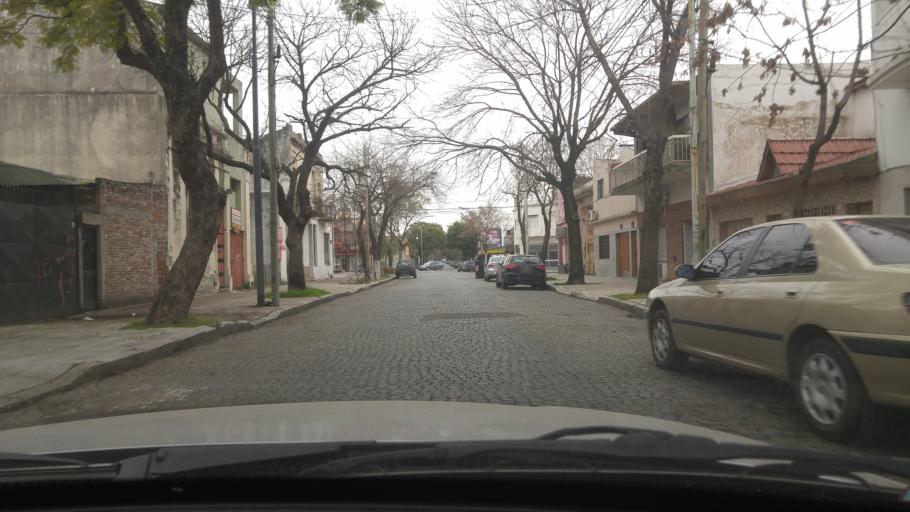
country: AR
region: Buenos Aires F.D.
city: Villa Santa Rita
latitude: -34.6335
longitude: -58.4965
